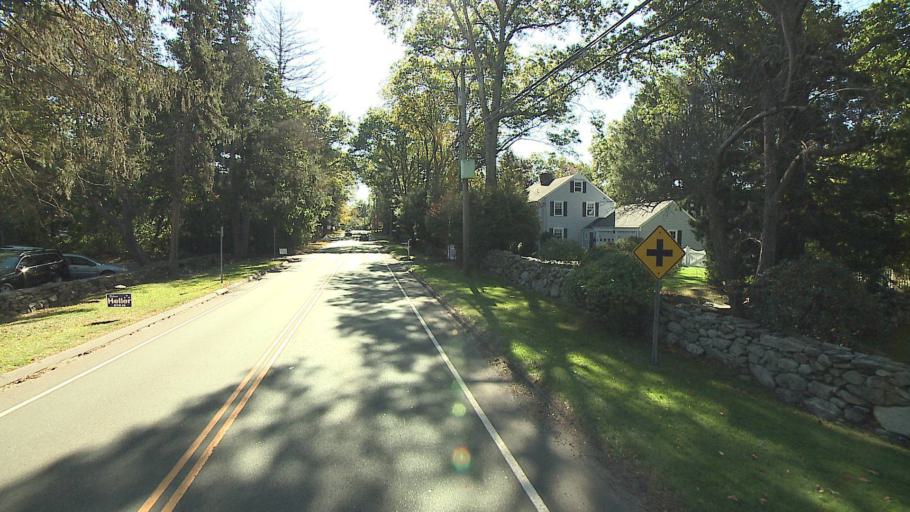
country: US
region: Connecticut
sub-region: Fairfield County
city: Westport
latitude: 41.1527
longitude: -73.3555
